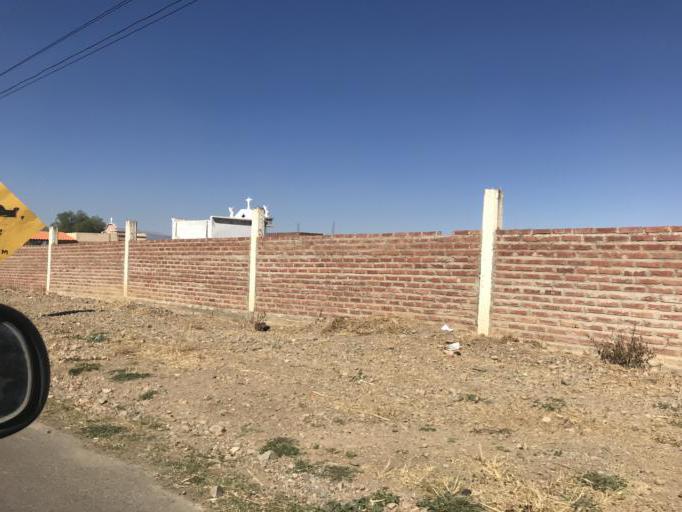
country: BO
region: Cochabamba
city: Tarata
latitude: -17.6037
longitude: -65.9880
